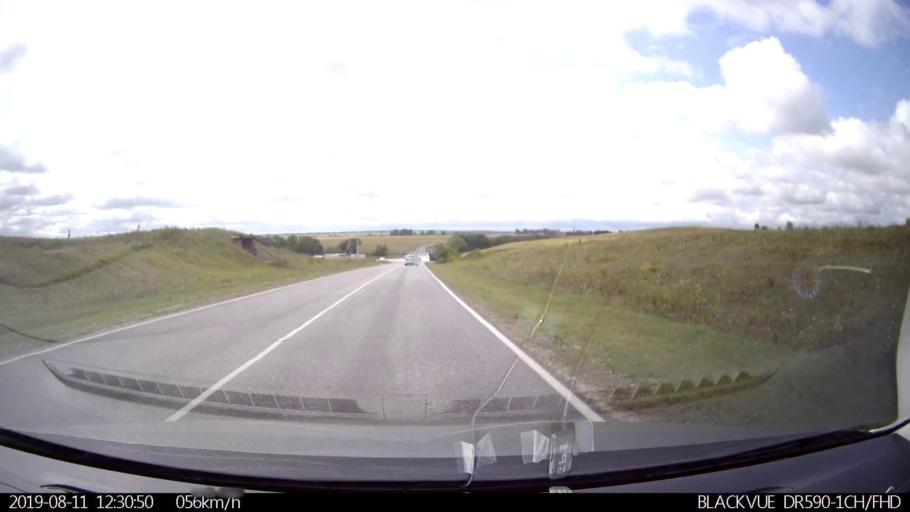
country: RU
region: Ulyanovsk
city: Ignatovka
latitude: 53.8231
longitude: 47.8907
